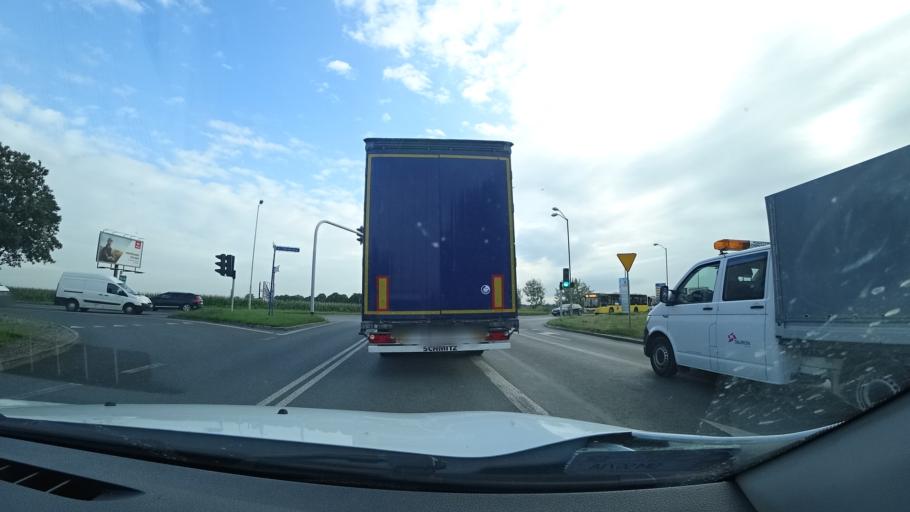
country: PL
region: Silesian Voivodeship
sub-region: Siemianowice Slaskie
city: Siemianowice Slaskie
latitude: 50.3305
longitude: 19.0106
